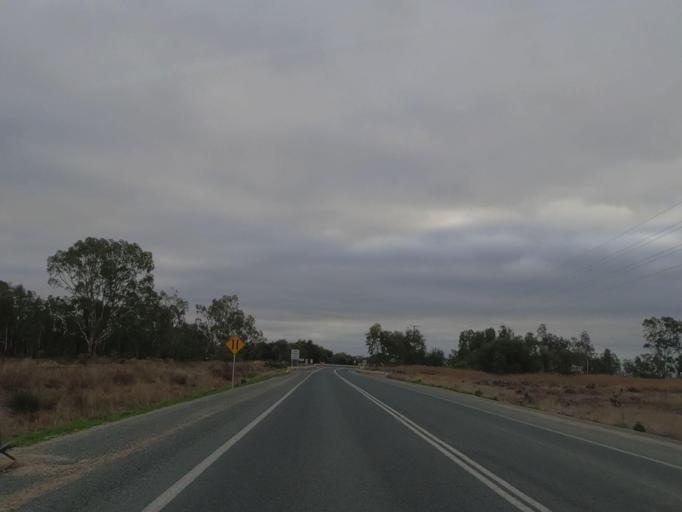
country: AU
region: Victoria
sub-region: Swan Hill
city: Swan Hill
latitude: -35.5369
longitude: 143.7469
